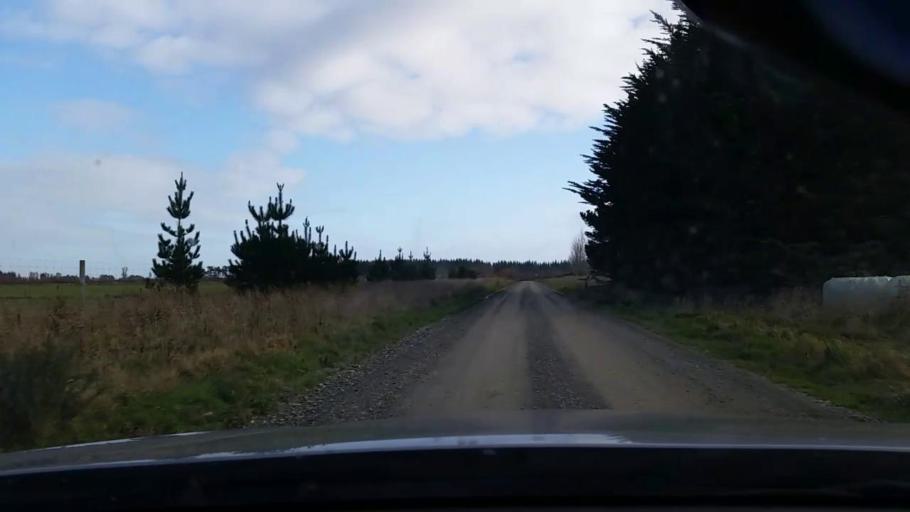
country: NZ
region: Southland
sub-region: Southland District
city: Winton
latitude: -46.2734
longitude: 168.2852
